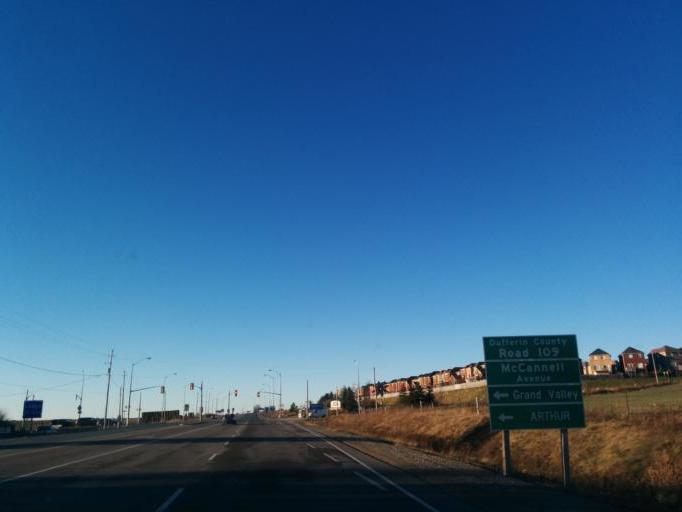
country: CA
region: Ontario
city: Orangeville
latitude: 43.9148
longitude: -80.0702
